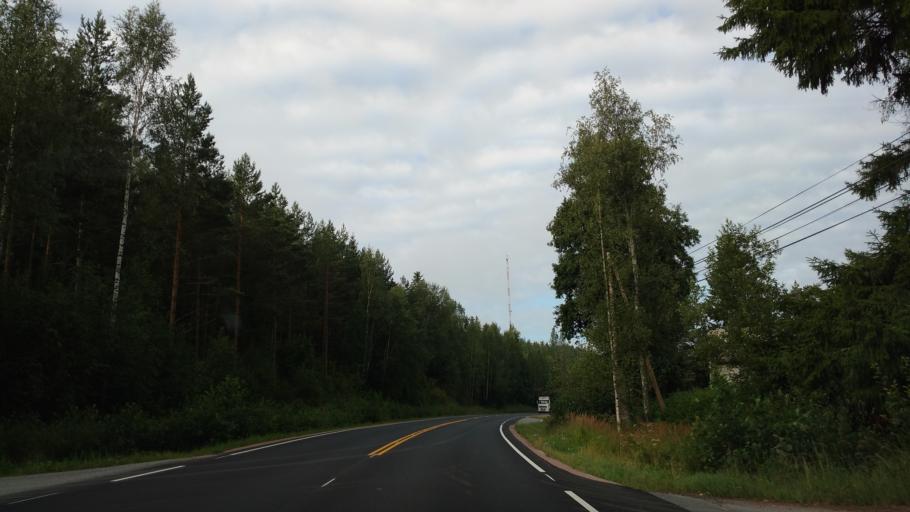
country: FI
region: Varsinais-Suomi
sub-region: Aboland-Turunmaa
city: Kimito
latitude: 60.1552
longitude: 22.7144
